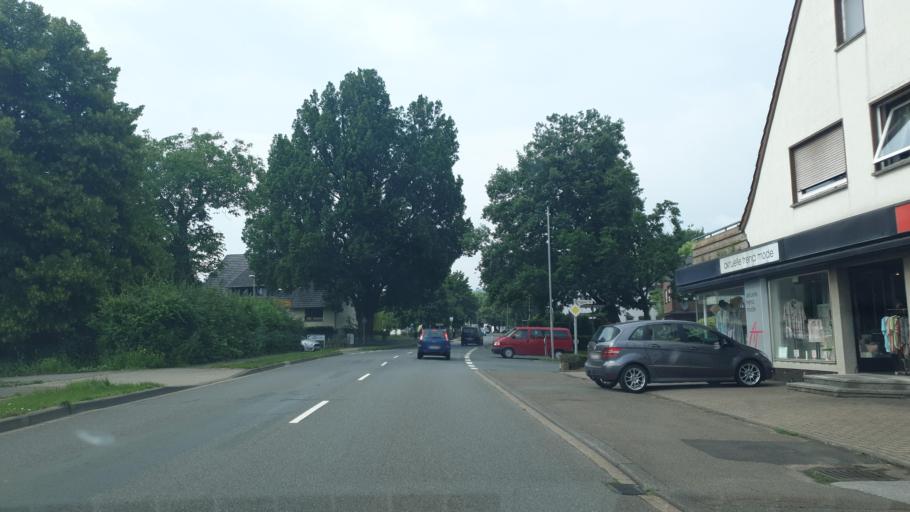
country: DE
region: North Rhine-Westphalia
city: Bad Oeynhausen
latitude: 52.2513
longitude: 8.7819
